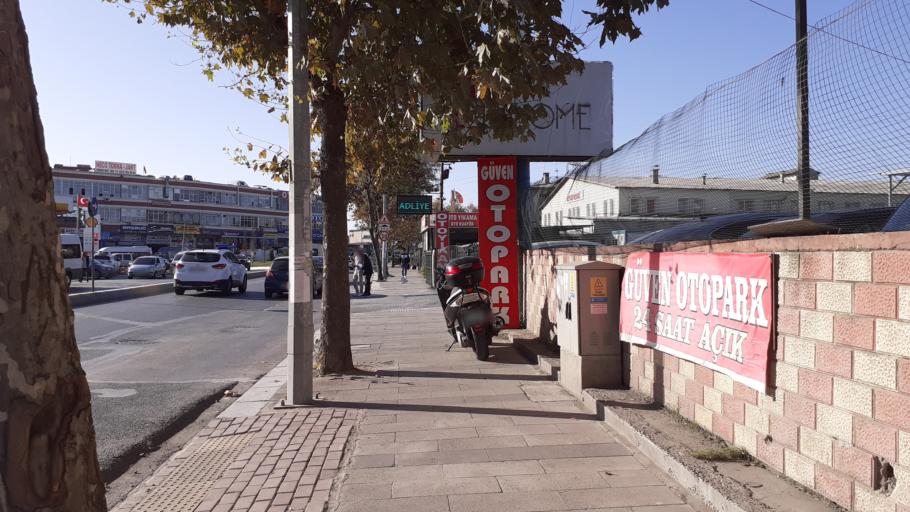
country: TR
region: Istanbul
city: Mahmutbey
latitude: 41.0103
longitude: 28.7952
